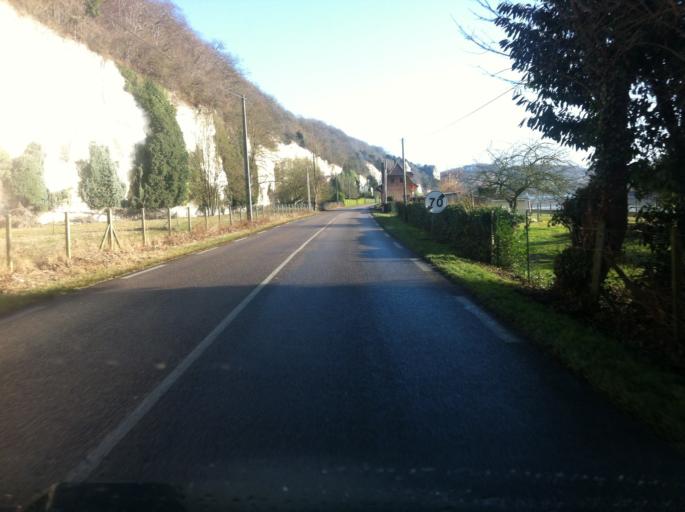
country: FR
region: Haute-Normandie
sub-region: Departement de la Seine-Maritime
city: Duclair
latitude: 49.4865
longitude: 0.9000
